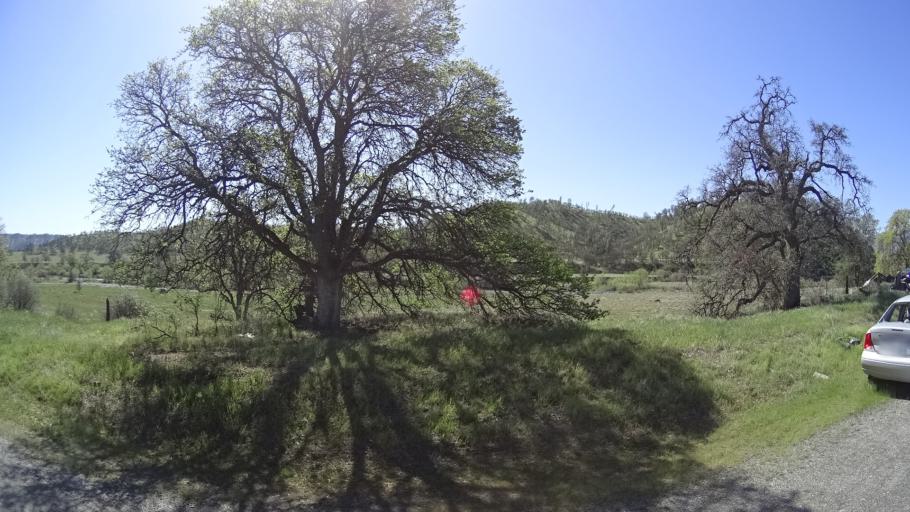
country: US
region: California
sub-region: Glenn County
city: Orland
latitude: 39.6741
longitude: -122.5179
